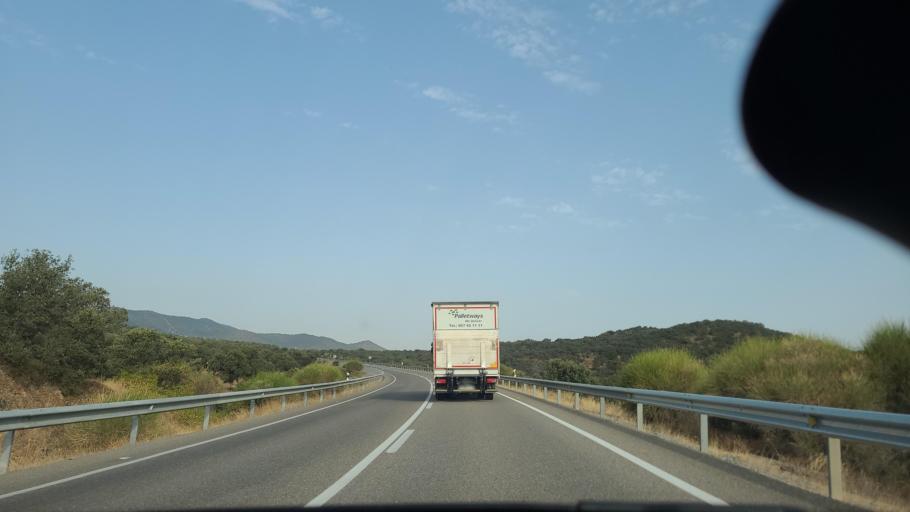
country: ES
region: Andalusia
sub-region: Province of Cordoba
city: Espiel
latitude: 38.2011
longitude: -5.1056
